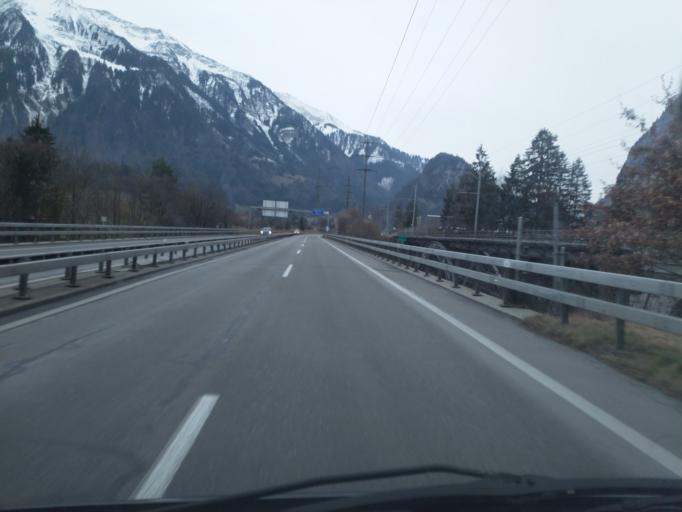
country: CH
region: Bern
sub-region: Frutigen-Niedersimmental District
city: Wimmis
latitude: 46.6876
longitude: 7.6454
